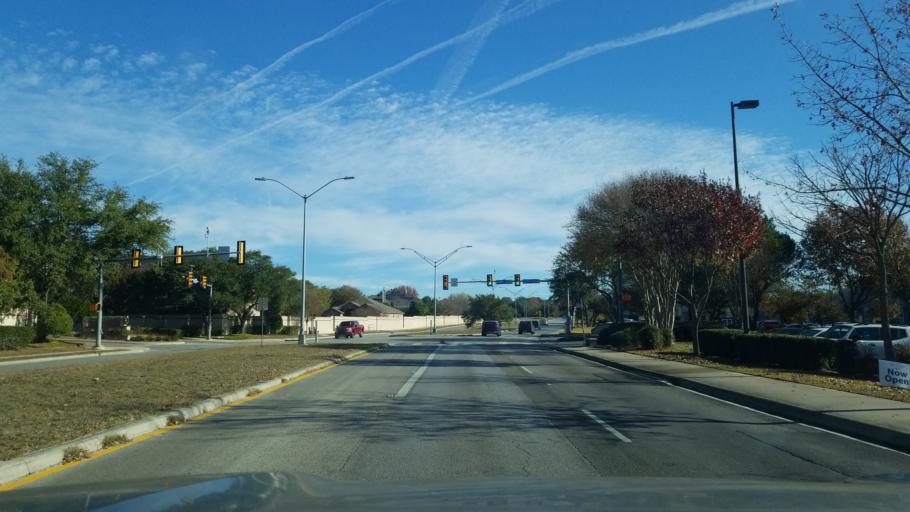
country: US
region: Texas
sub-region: Bexar County
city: Shavano Park
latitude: 29.5848
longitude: -98.5344
